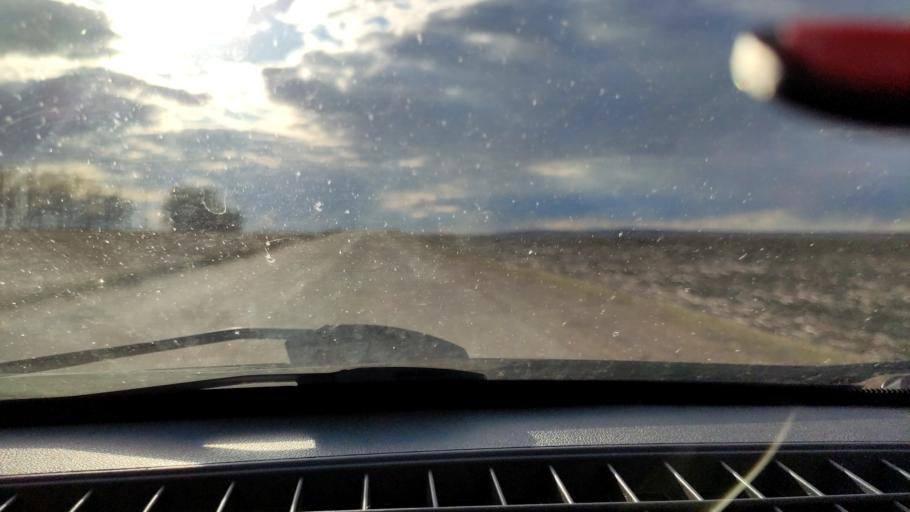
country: RU
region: Bashkortostan
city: Karmaskaly
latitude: 54.3483
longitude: 56.0679
